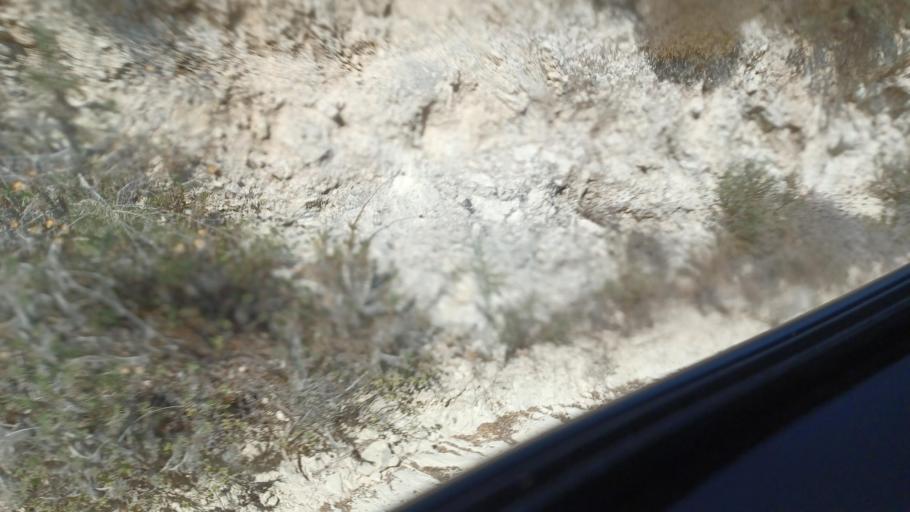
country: CY
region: Pafos
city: Tala
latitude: 34.8696
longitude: 32.4483
